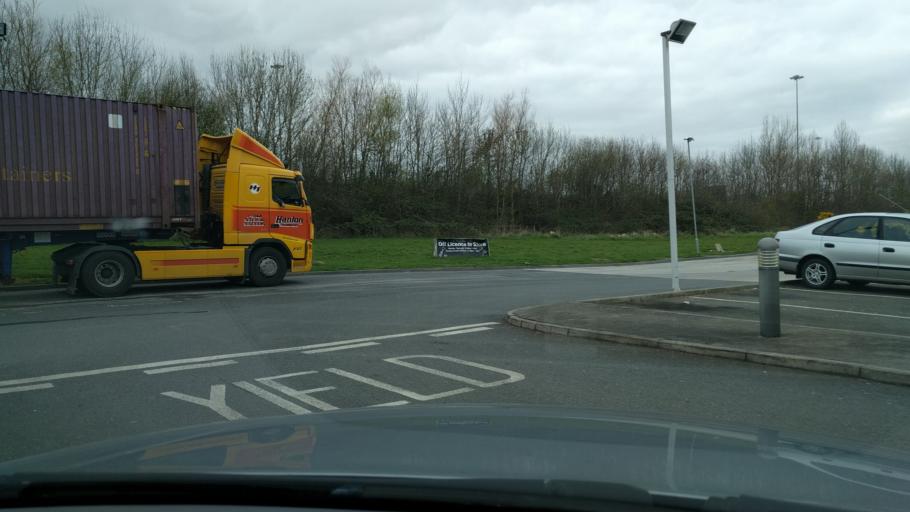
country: IE
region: Leinster
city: Balrothery
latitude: 53.5646
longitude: -6.2119
